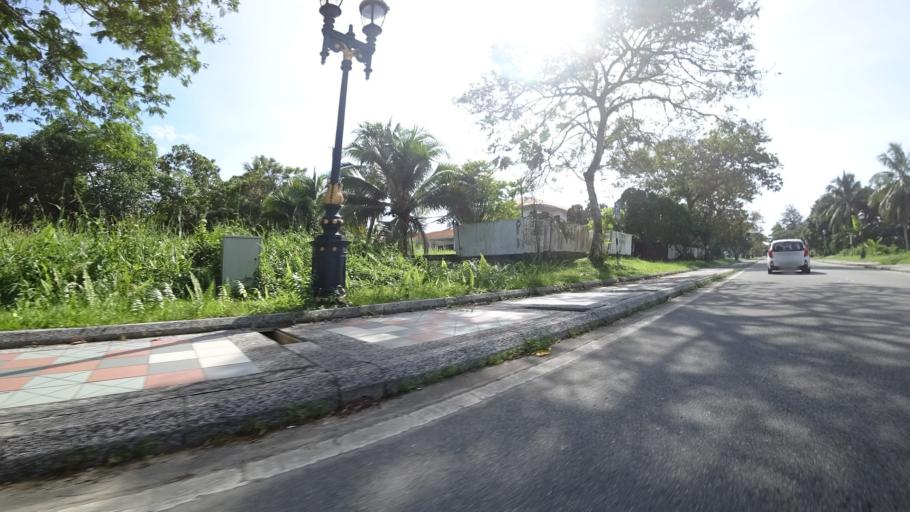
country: BN
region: Brunei and Muara
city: Bandar Seri Begawan
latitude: 4.9371
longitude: 114.8412
